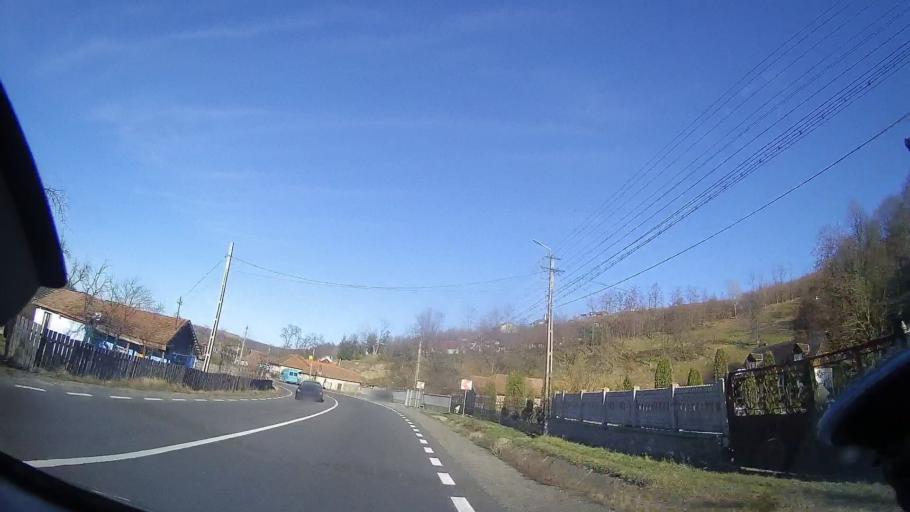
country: RO
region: Cluj
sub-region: Comuna Poeni
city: Poeni
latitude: 46.9098
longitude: 22.8658
